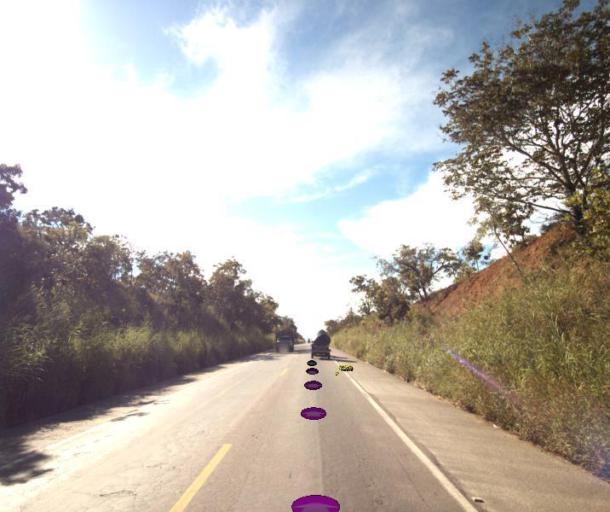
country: BR
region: Goias
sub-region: Rialma
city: Rialma
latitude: -15.4877
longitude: -49.4910
